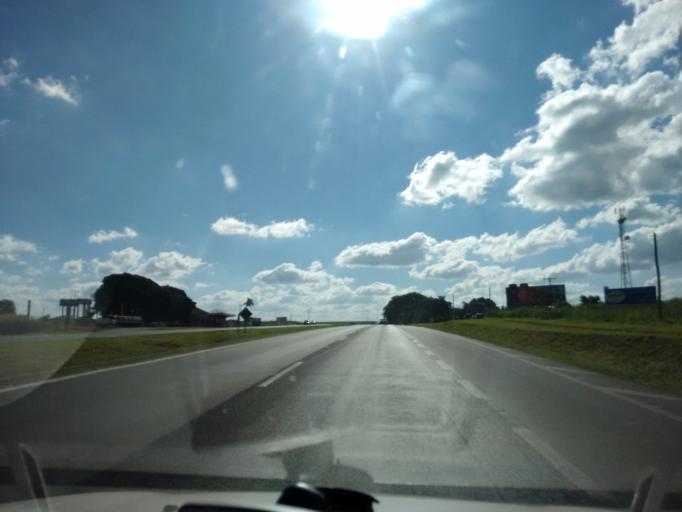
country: BR
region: Sao Paulo
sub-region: Araraquara
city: Araraquara
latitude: -21.8744
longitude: -48.1002
